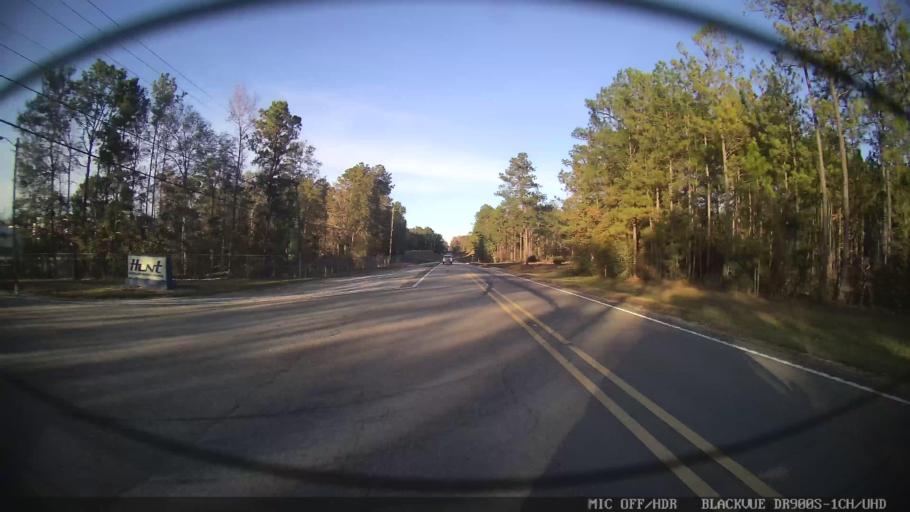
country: US
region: Mississippi
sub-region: Lamar County
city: Lumberton
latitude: 31.0249
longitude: -89.4479
